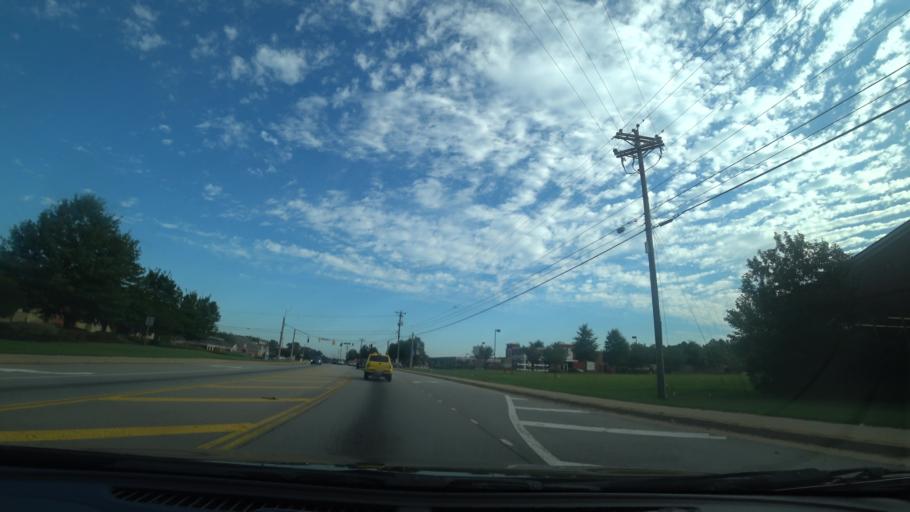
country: US
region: Georgia
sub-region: Rockdale County
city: Conyers
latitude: 33.6240
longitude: -83.9765
